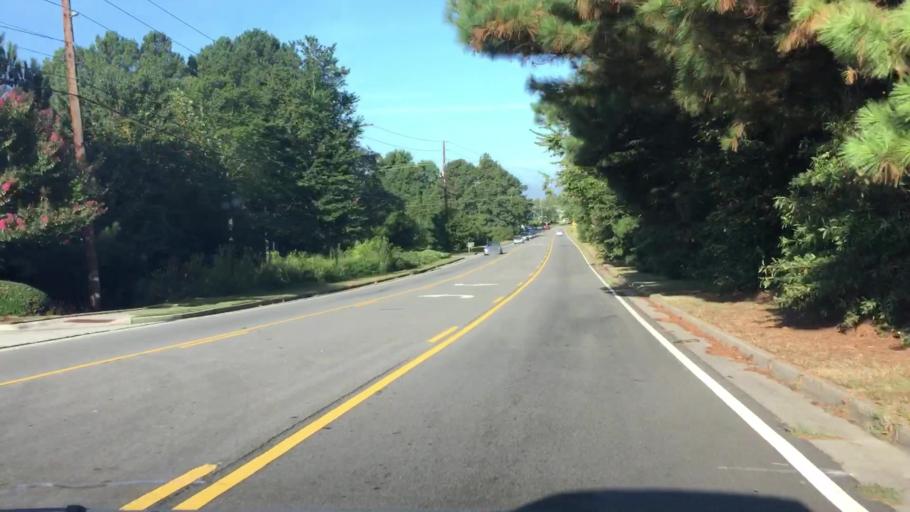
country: US
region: Georgia
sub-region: Clayton County
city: Morrow
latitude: 33.5602
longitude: -84.3178
